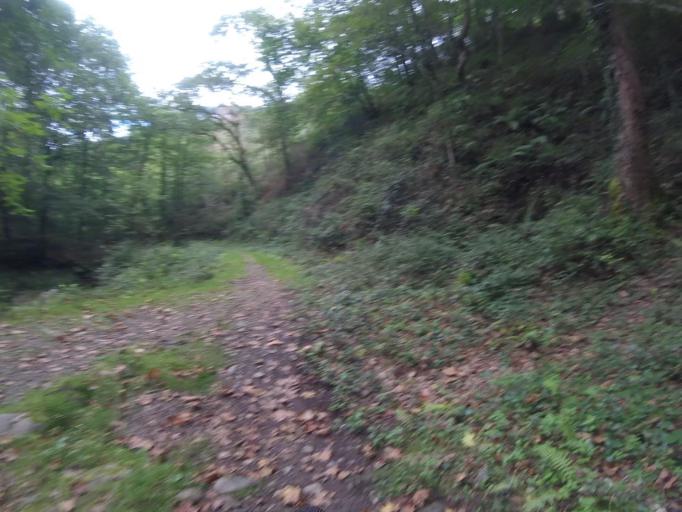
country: ES
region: Basque Country
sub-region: Provincia de Guipuzcoa
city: Errenteria
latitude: 43.2712
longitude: -1.8397
